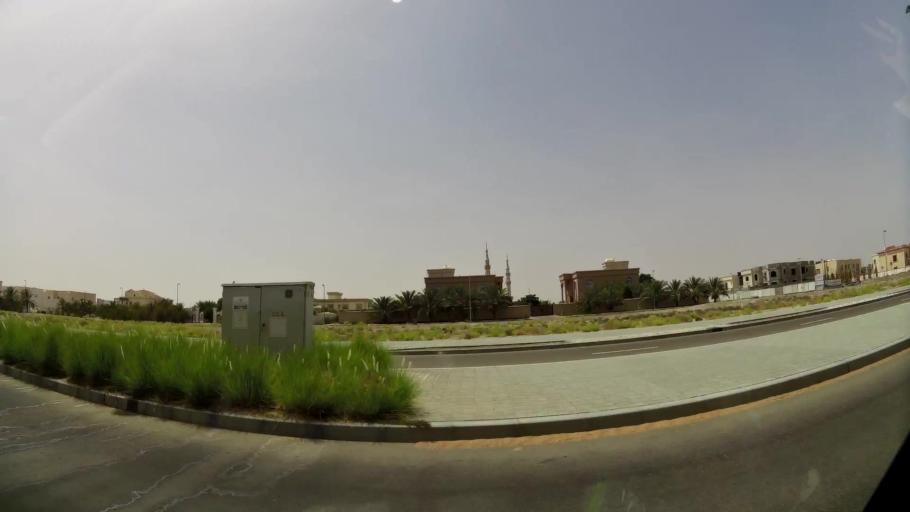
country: AE
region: Abu Dhabi
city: Al Ain
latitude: 24.1387
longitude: 55.6374
